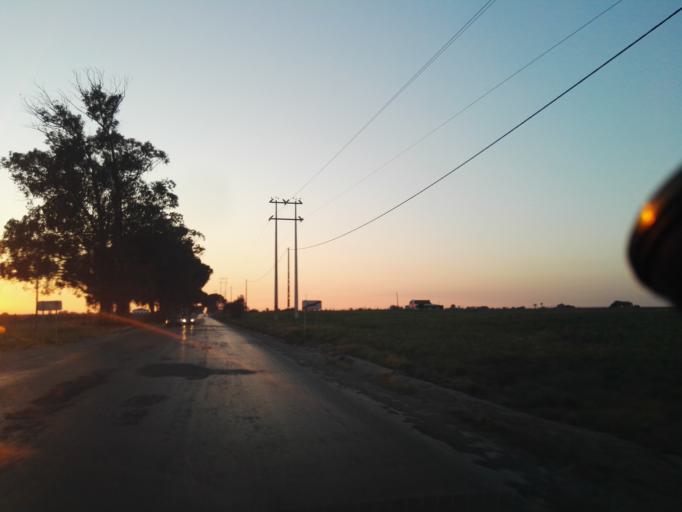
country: PT
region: Santarem
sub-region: Benavente
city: Poceirao
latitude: 38.6931
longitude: -8.7639
